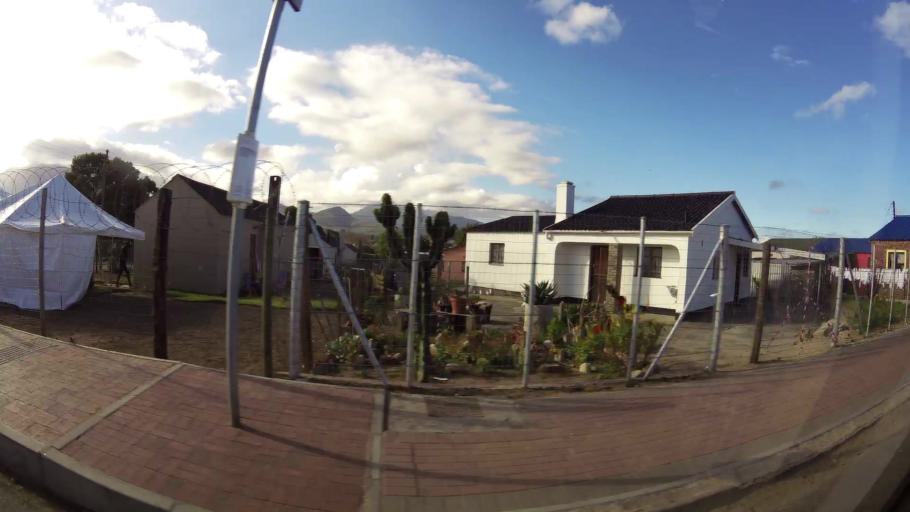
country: ZA
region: Western Cape
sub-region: Eden District Municipality
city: George
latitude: -33.9756
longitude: 22.4831
